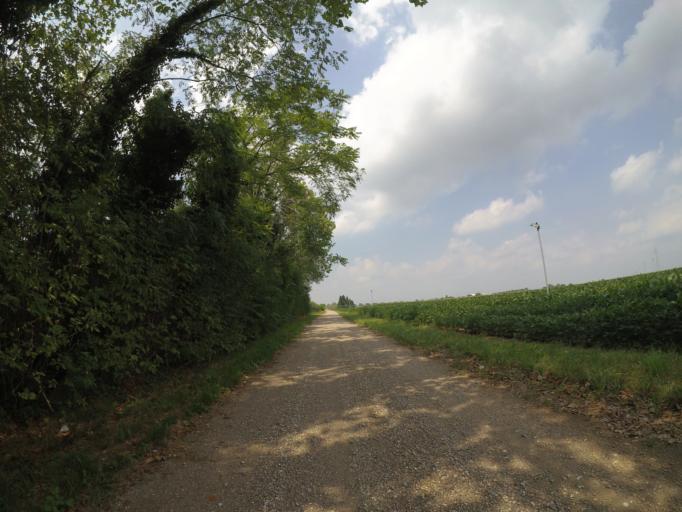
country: IT
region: Friuli Venezia Giulia
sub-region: Provincia di Udine
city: Codroipo
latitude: 45.9829
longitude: 13.0007
